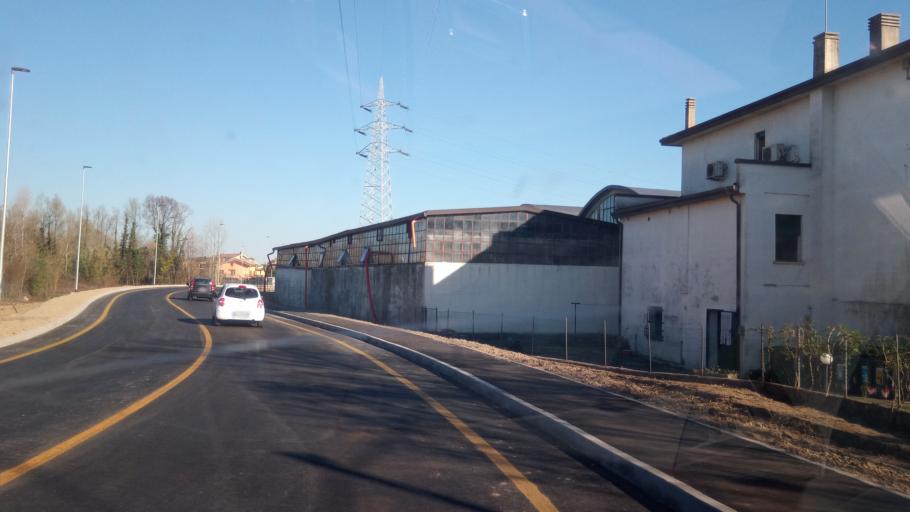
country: IT
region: Veneto
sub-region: Provincia di Padova
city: Padova
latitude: 45.4195
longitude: 11.9092
